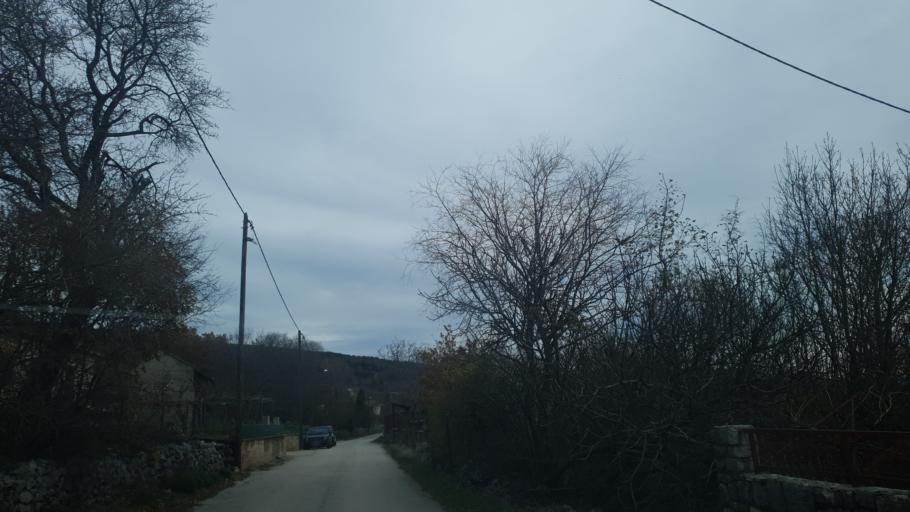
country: HR
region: Splitsko-Dalmatinska
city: Imotski
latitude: 43.4463
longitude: 17.2391
